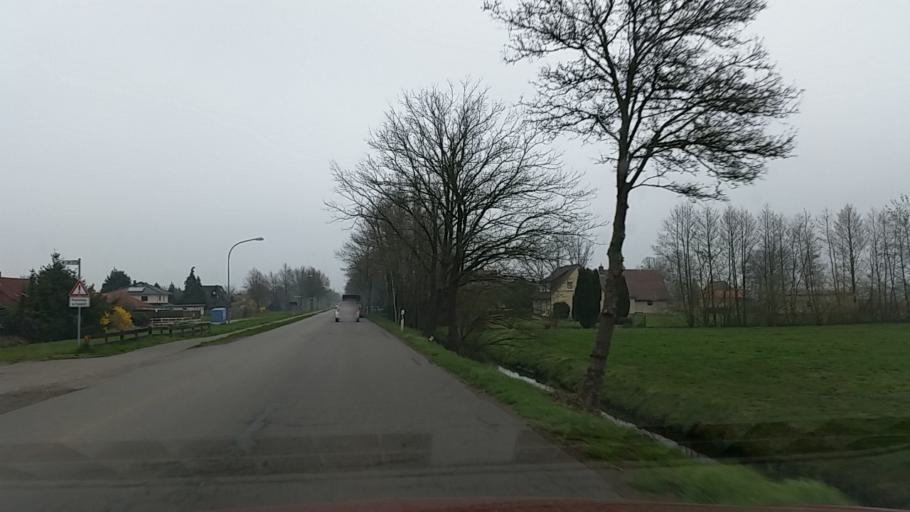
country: DE
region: Lower Saxony
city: Sassenburg
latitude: 52.5200
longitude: 10.5892
